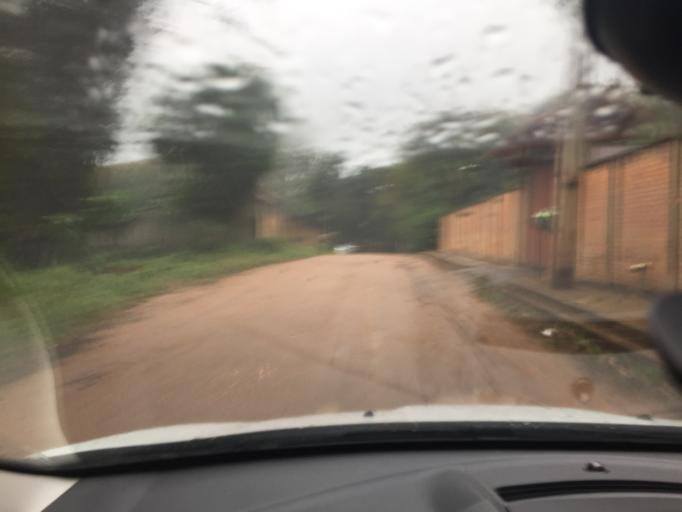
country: BR
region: Sao Paulo
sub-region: Jarinu
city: Jarinu
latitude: -23.1420
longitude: -46.7400
